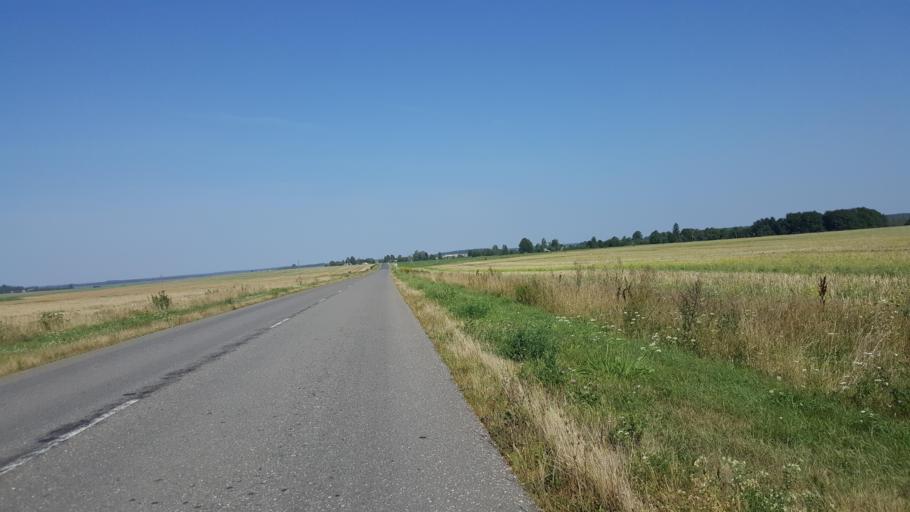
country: BY
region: Brest
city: Kamyanyets
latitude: 52.4565
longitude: 23.7246
